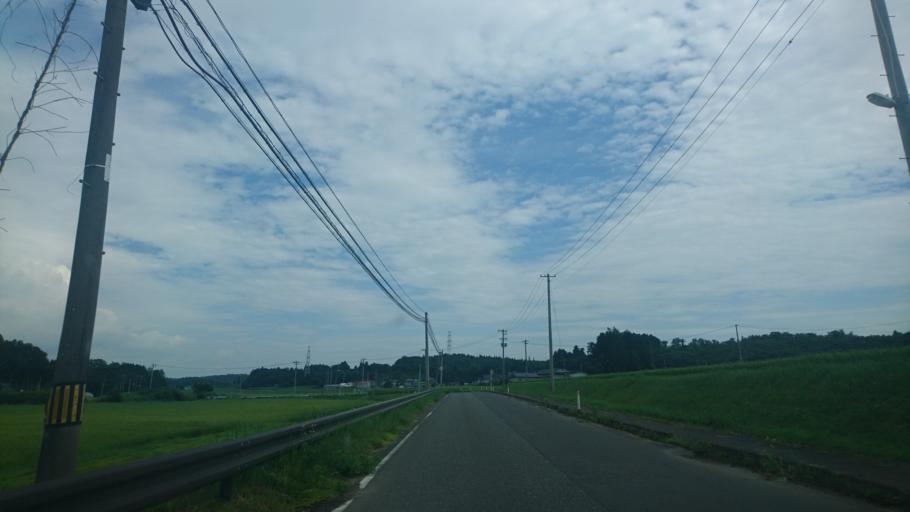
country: JP
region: Miyagi
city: Furukawa
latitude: 38.7652
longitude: 140.9671
